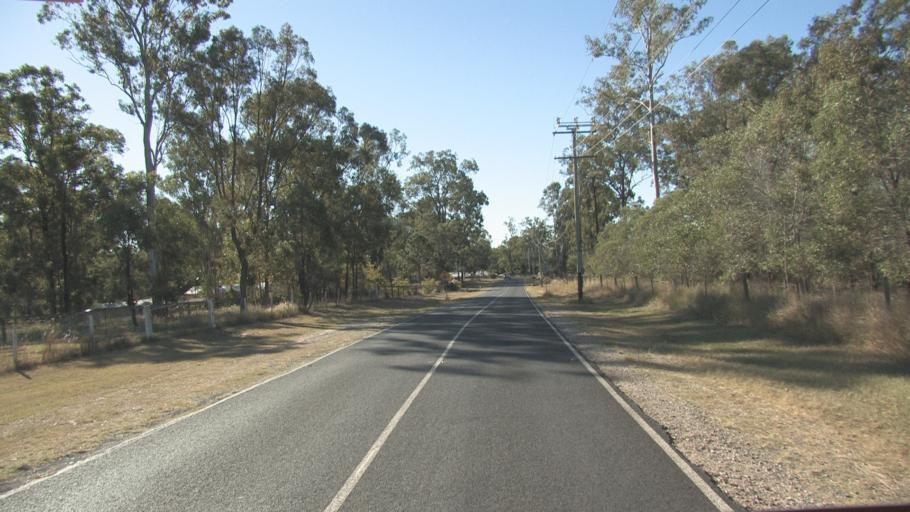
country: AU
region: Queensland
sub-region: Logan
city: Park Ridge South
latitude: -27.7380
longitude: 153.0175
